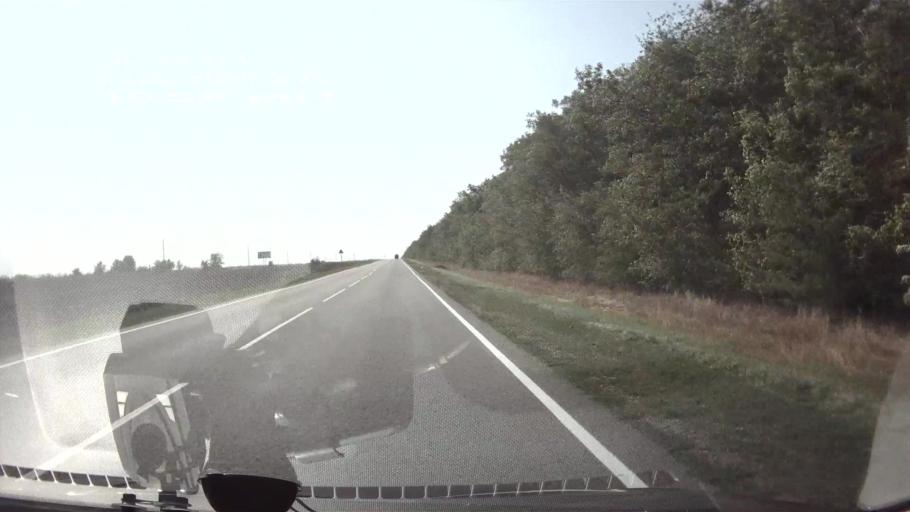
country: RU
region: Krasnodarskiy
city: Novopokrovskaya
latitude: 45.8790
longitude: 40.7208
